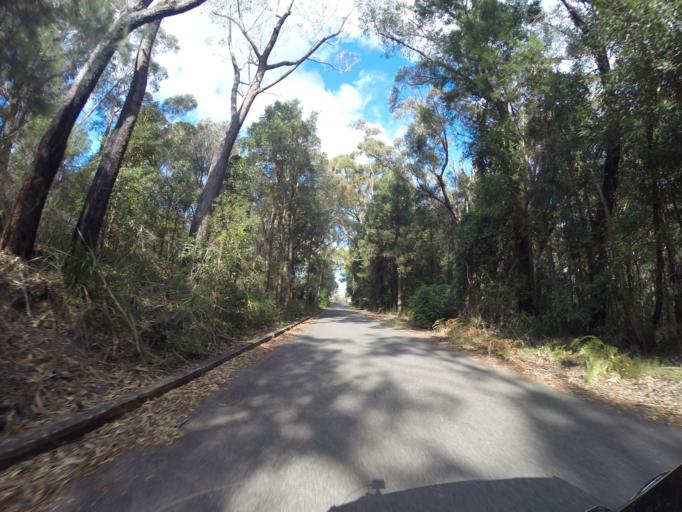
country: AU
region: New South Wales
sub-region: Wollongong
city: Mount Keira
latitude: -34.4013
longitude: 150.8559
